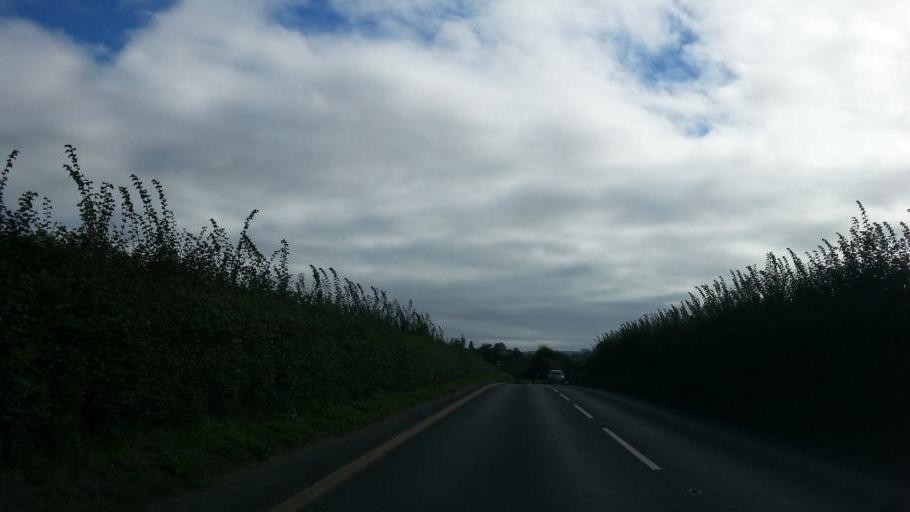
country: GB
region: England
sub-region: Herefordshire
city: Ross on Wye
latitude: 51.9123
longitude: -2.5519
